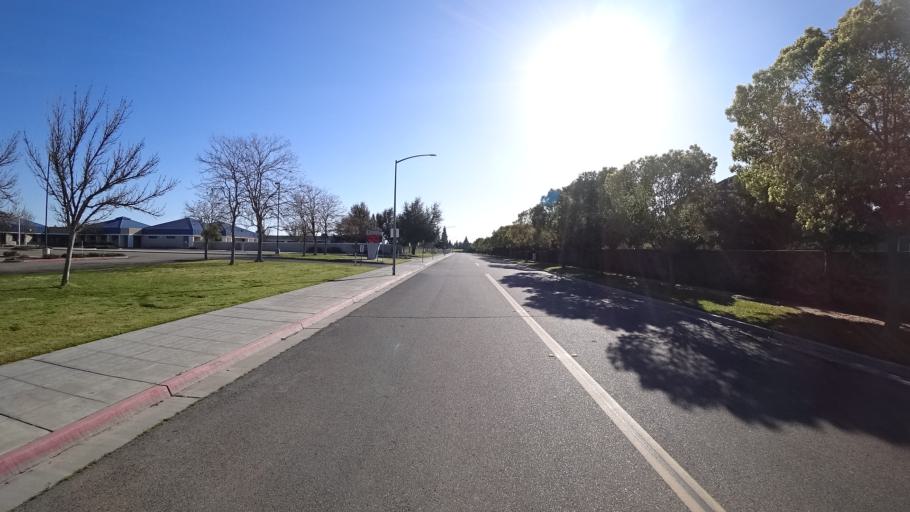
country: US
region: California
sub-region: Fresno County
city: Biola
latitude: 36.8334
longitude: -119.9040
